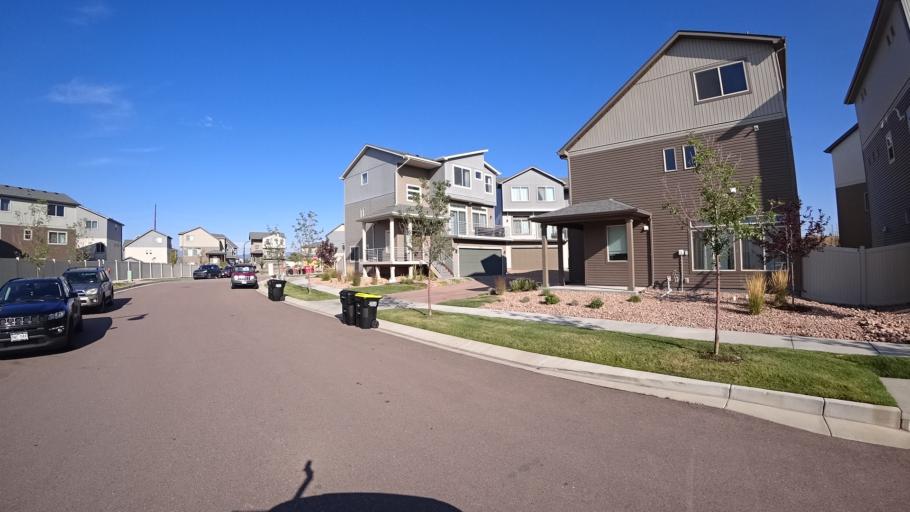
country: US
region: Colorado
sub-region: El Paso County
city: Cimarron Hills
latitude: 38.9294
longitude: -104.6607
